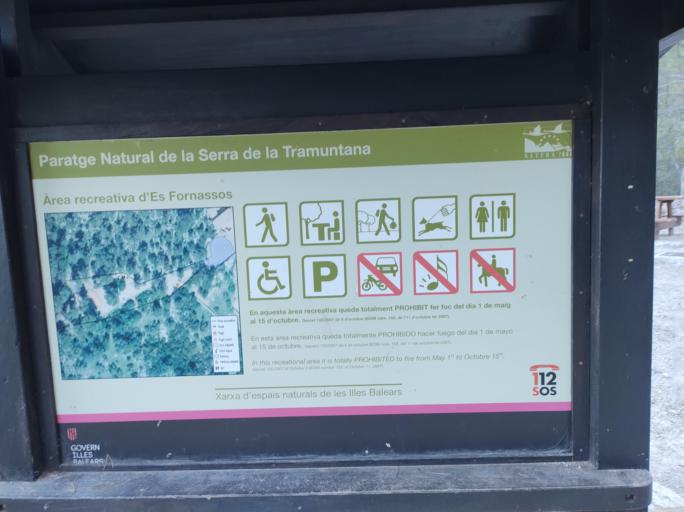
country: ES
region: Balearic Islands
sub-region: Illes Balears
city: Selva
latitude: 39.7696
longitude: 2.8985
